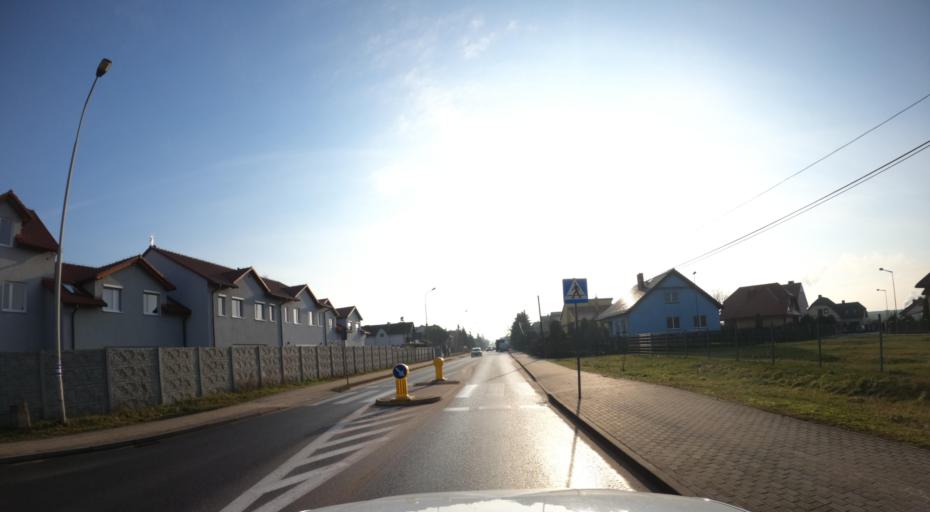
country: PL
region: Lubusz
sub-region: Powiat gorzowski
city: Kostrzyn nad Odra
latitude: 52.6050
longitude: 14.6353
